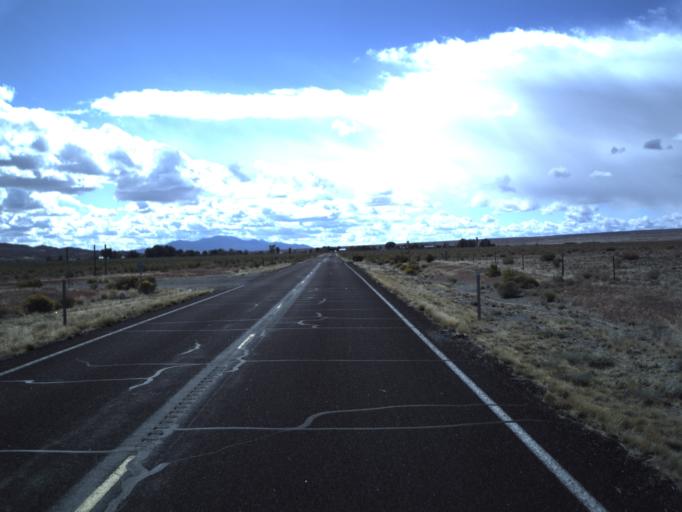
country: US
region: Nevada
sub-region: White Pine County
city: McGill
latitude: 38.9549
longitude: -114.0334
